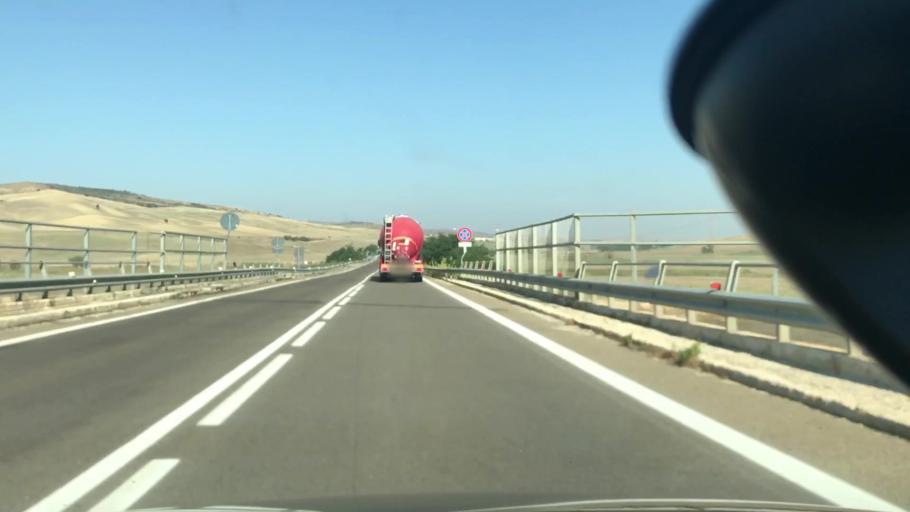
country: IT
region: Basilicate
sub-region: Provincia di Matera
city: Irsina
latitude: 40.7900
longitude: 16.2853
